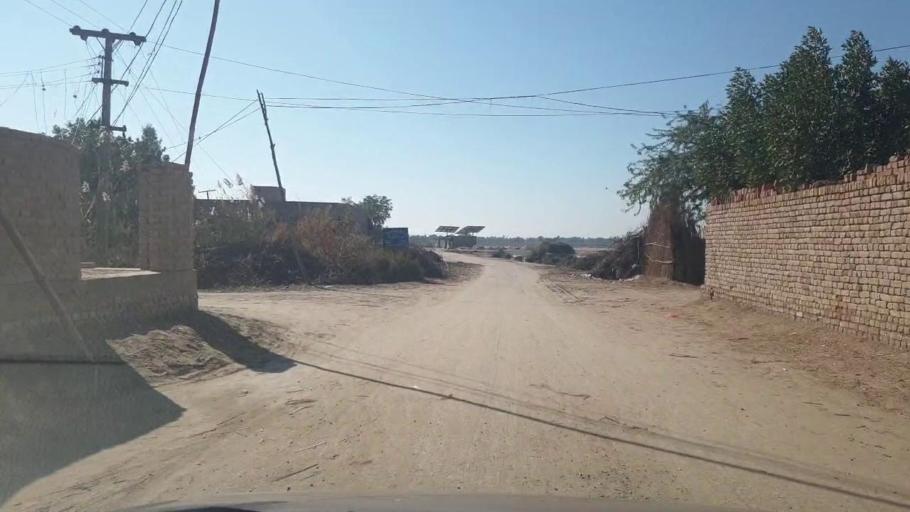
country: PK
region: Sindh
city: Bozdar
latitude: 27.1349
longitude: 68.6425
